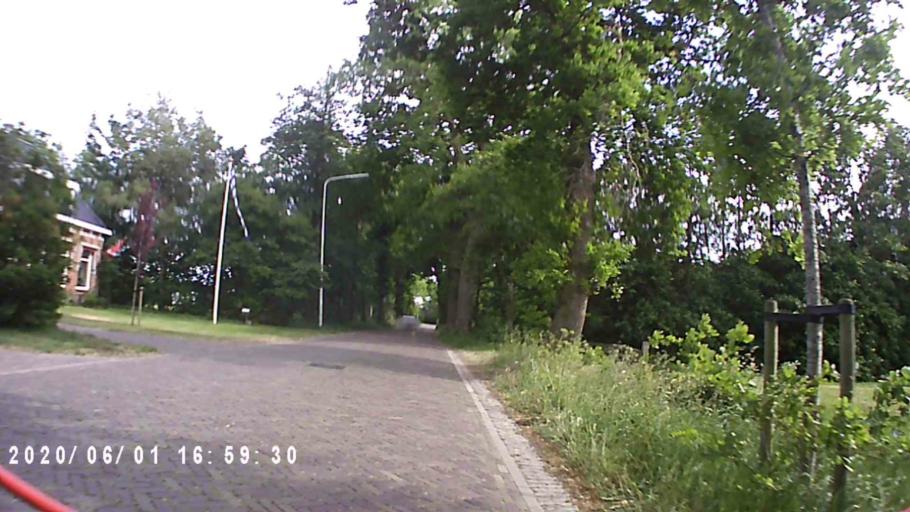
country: NL
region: Friesland
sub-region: Gemeente Tytsjerksteradiel
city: Hurdegaryp
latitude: 53.1860
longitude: 5.9282
